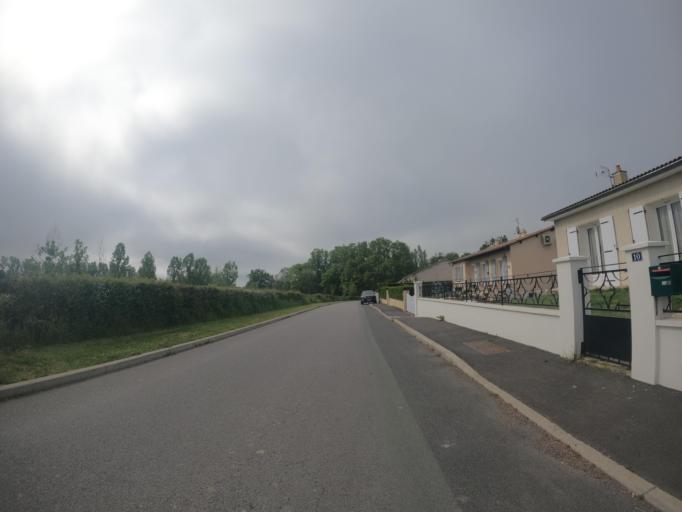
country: FR
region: Poitou-Charentes
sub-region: Departement des Deux-Sevres
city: Chiche
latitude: 46.8303
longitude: -0.3592
